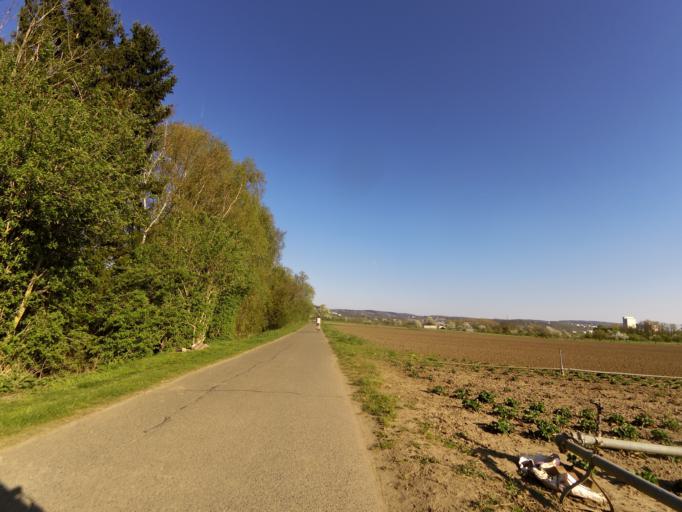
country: DE
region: Rheinland-Pfalz
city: Weitersburg
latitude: 50.4022
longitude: 7.5930
